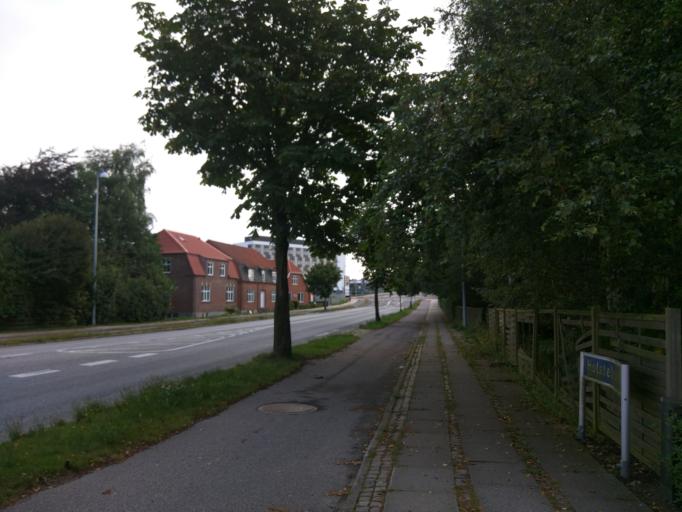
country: DK
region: Central Jutland
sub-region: Viborg Kommune
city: Viborg
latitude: 56.4492
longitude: 9.3862
